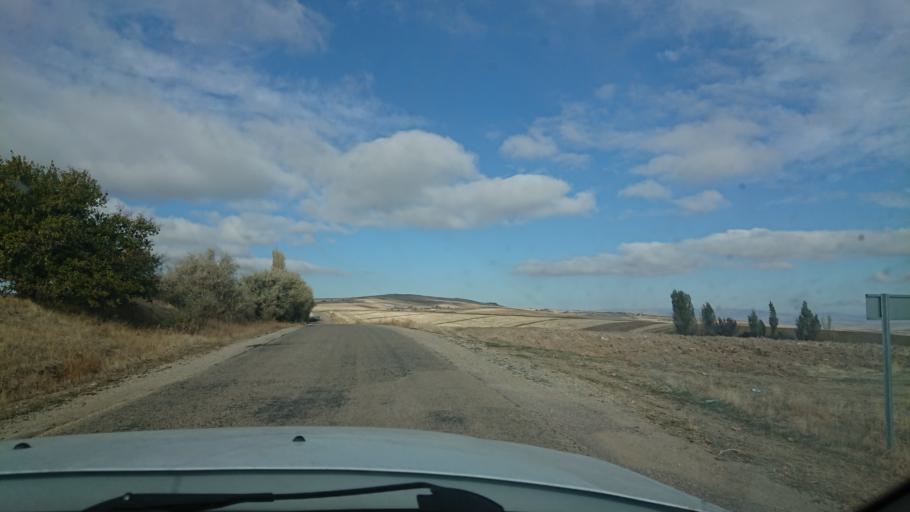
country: TR
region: Aksaray
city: Agacoren
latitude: 38.8144
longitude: 33.9827
